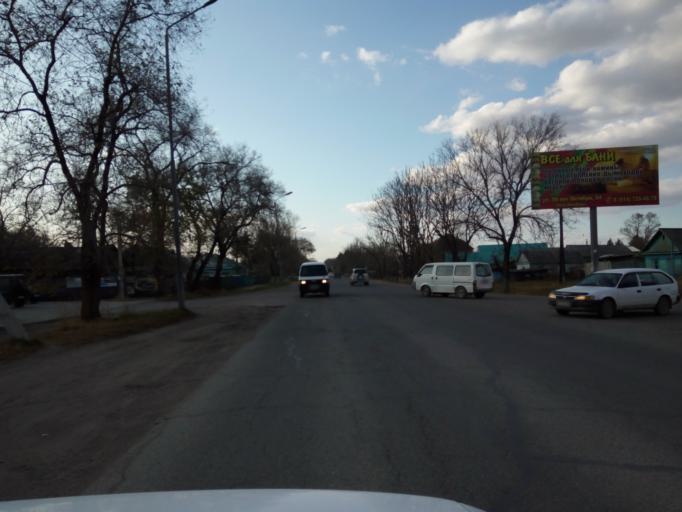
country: RU
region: Primorskiy
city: Dal'nerechensk
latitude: 45.9216
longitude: 133.7509
